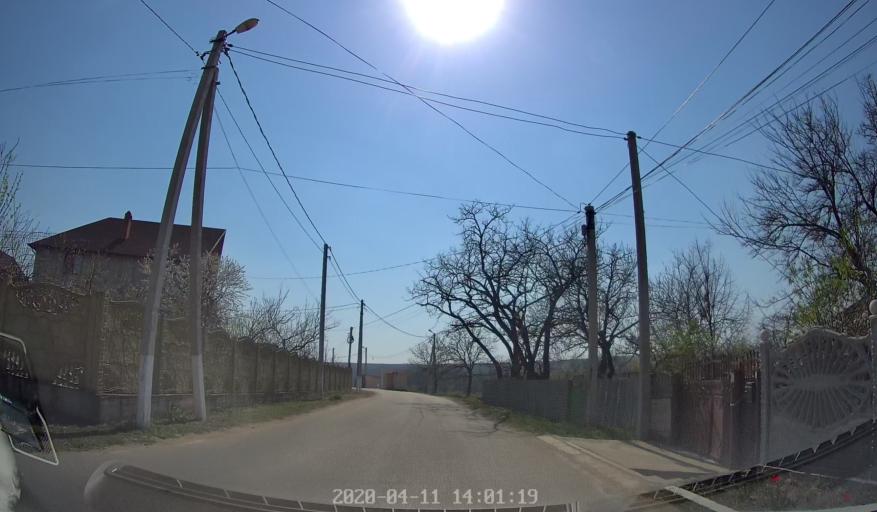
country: MD
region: Chisinau
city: Vadul lui Voda
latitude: 47.0825
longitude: 29.1312
